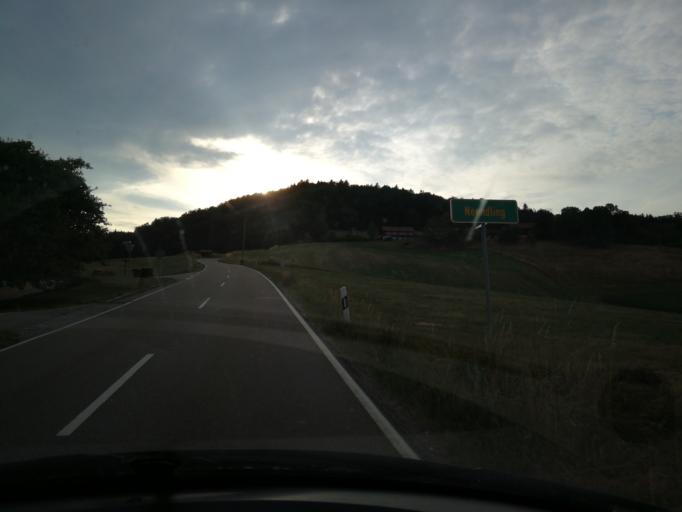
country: DE
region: Bavaria
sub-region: Lower Bavaria
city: Falkenfels
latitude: 49.0449
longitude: 12.6166
